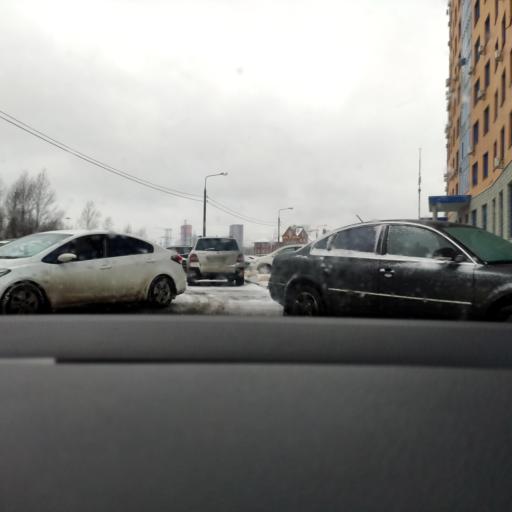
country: RU
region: Moscow
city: Ivanovskoye
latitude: 55.7742
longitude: 37.8460
